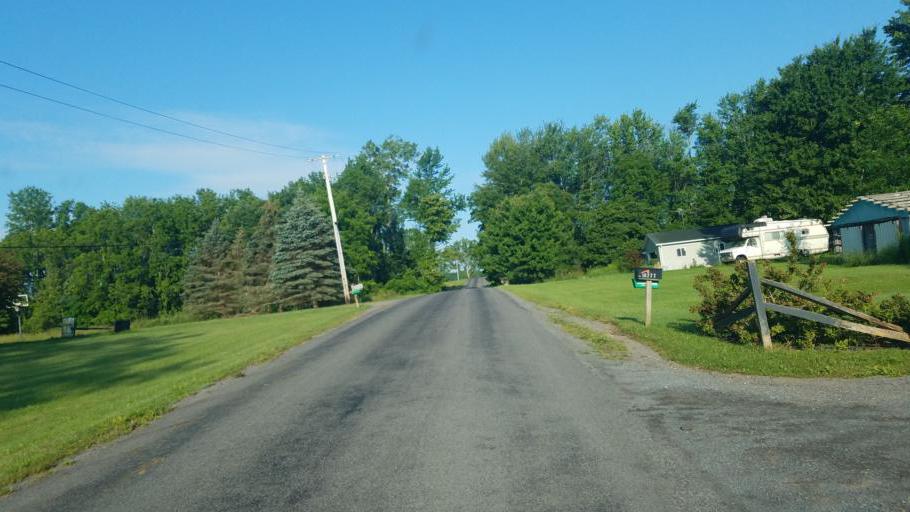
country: US
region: New York
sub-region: Wayne County
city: Clyde
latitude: 43.0446
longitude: -76.8723
